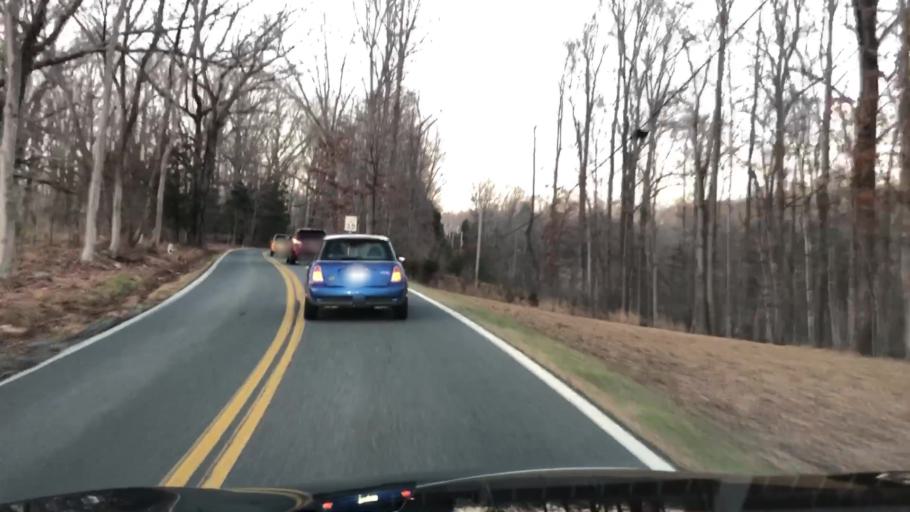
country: US
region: Virginia
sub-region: City of Lynchburg
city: West Lynchburg
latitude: 37.4265
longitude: -79.2490
